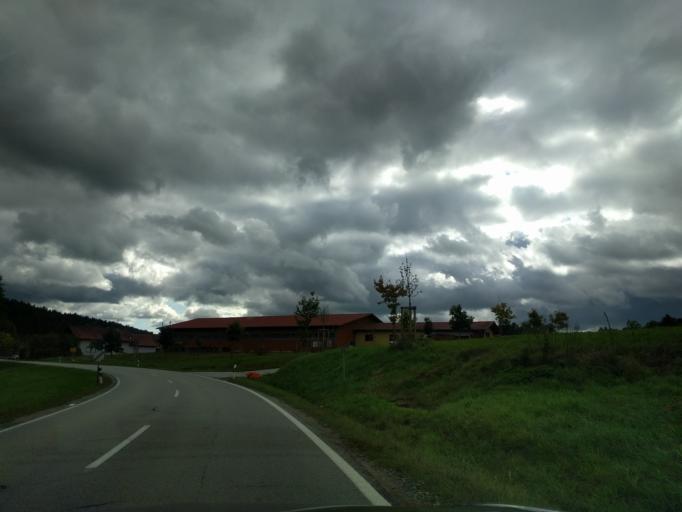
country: DE
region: Bavaria
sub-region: Lower Bavaria
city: Auerbach
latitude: 48.8264
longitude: 13.0909
